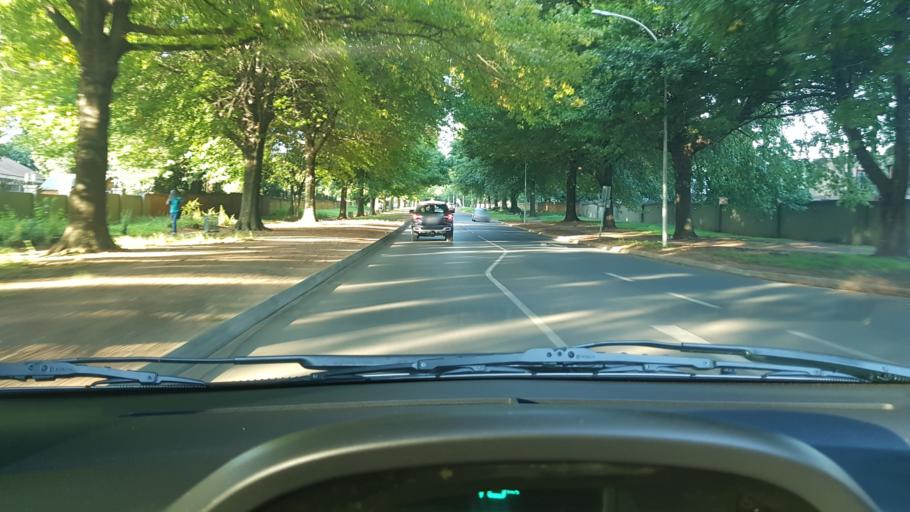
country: ZA
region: Gauteng
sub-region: Ekurhuleni Metropolitan Municipality
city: Germiston
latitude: -26.1740
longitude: 28.1414
